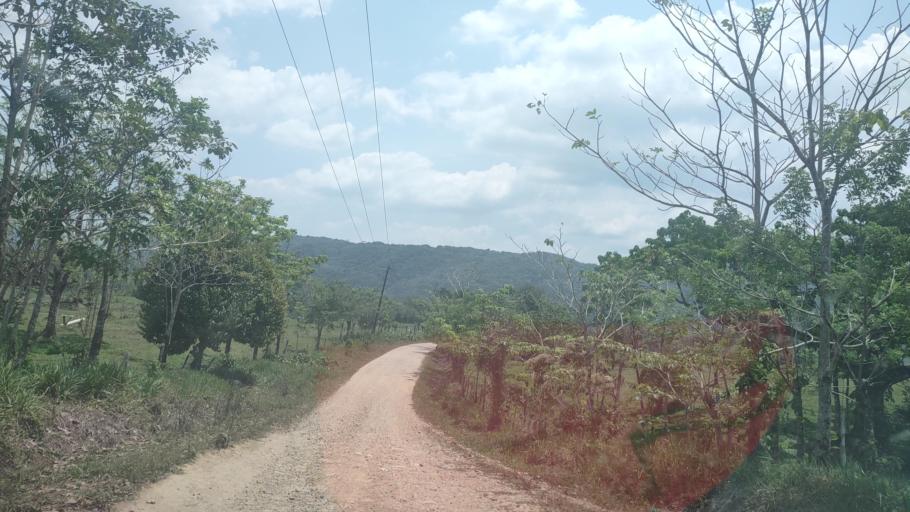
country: MX
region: Chiapas
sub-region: Tecpatan
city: Raudales Malpaso
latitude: 17.2793
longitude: -93.8699
